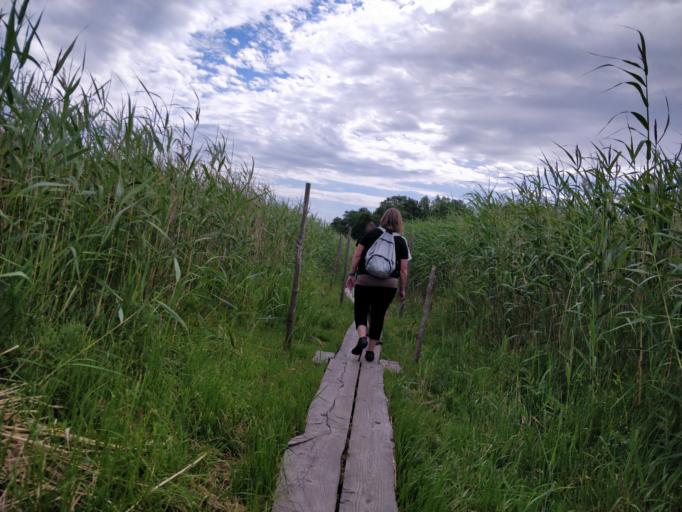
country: FI
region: Uusimaa
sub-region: Helsinki
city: Helsinki
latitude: 60.2063
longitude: 24.9958
